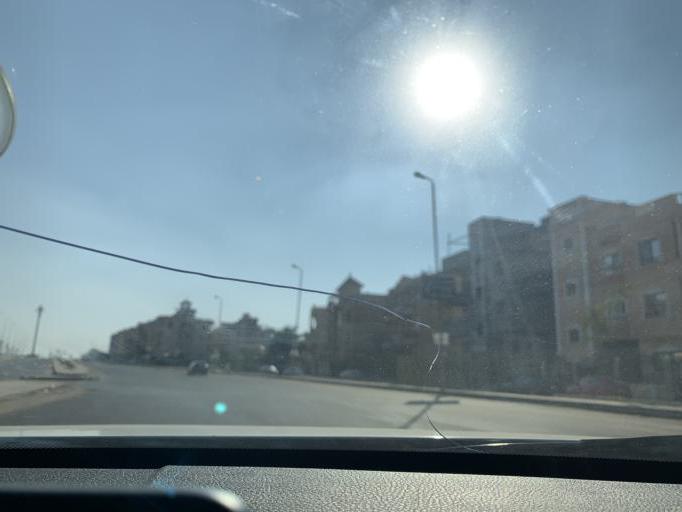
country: EG
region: Muhafazat al Qalyubiyah
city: Al Khankah
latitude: 30.0036
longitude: 31.4805
